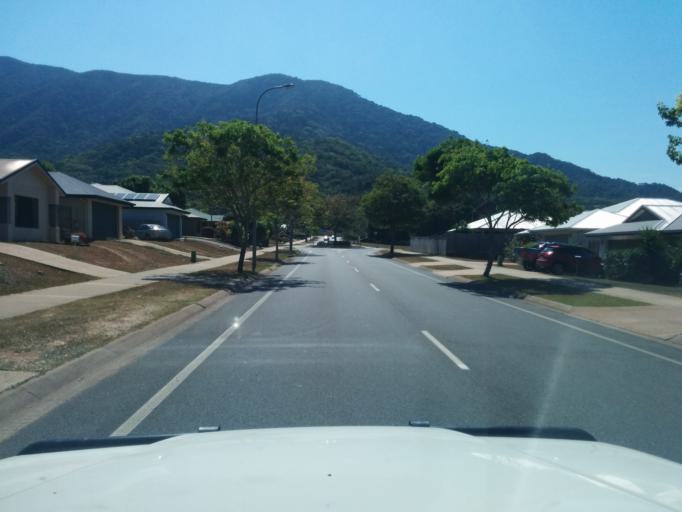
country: AU
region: Queensland
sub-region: Cairns
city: Redlynch
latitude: -16.8949
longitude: 145.6977
